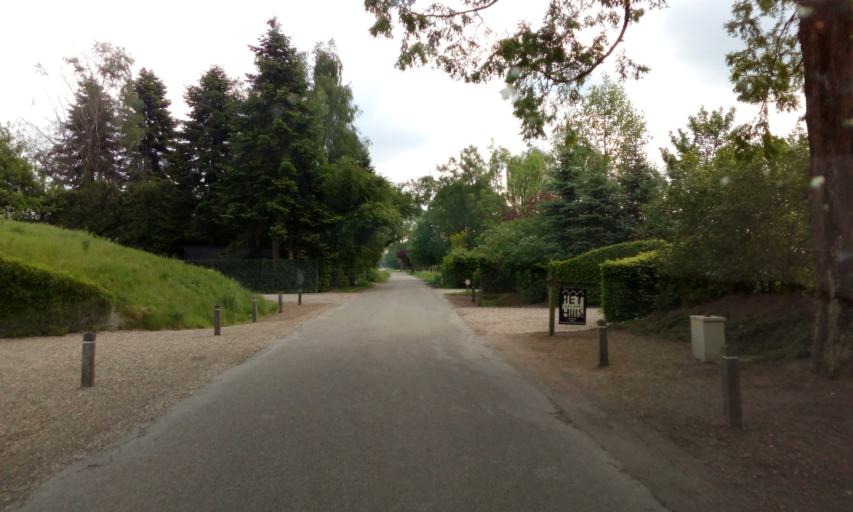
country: NL
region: Gelderland
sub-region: Gemeente Voorst
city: Voorst
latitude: 52.1640
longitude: 6.0826
